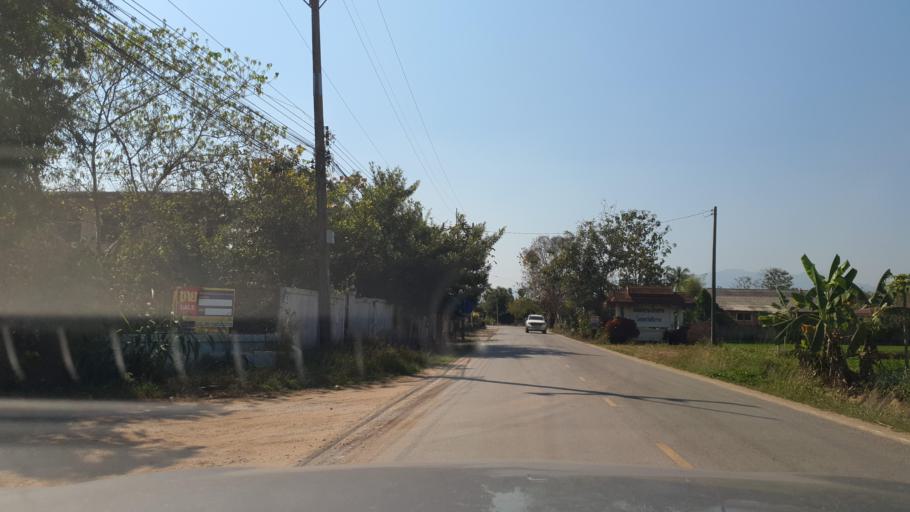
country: TH
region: Chiang Rai
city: Mae Lao
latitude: 19.7635
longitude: 99.7223
